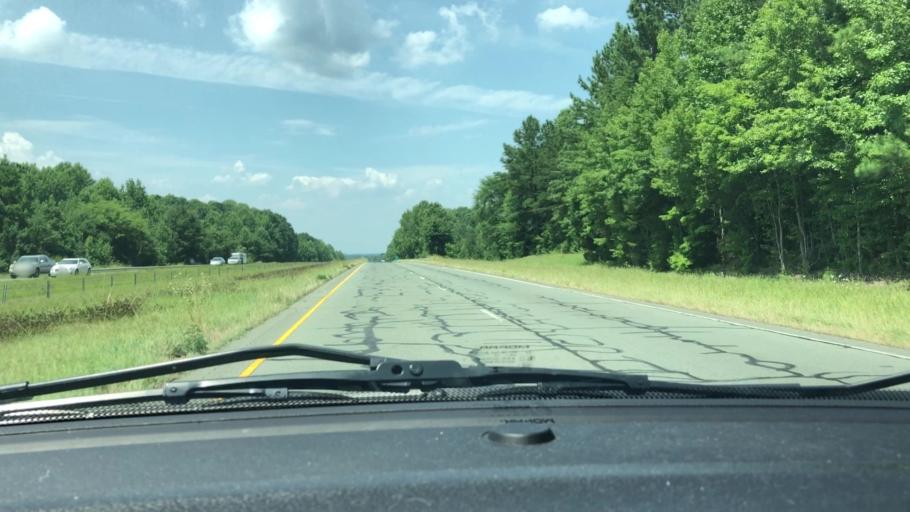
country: US
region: North Carolina
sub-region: Chatham County
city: Siler City
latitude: 35.7111
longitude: -79.4289
